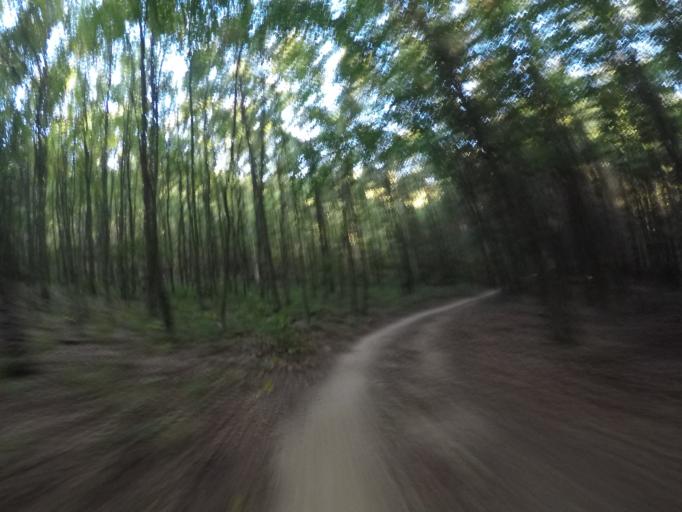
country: SK
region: Kosicky
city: Kosice
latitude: 48.7506
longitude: 21.1860
